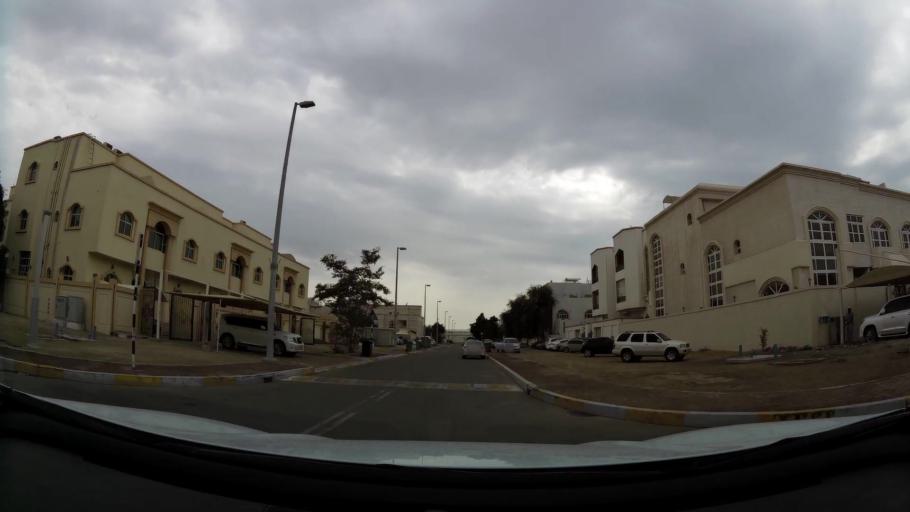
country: AE
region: Abu Dhabi
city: Abu Dhabi
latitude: 24.4258
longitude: 54.4255
